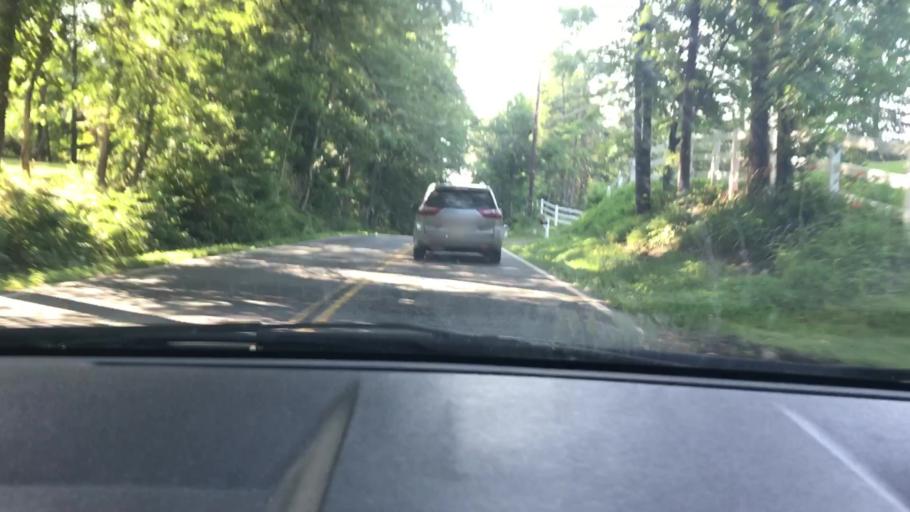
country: US
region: Virginia
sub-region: Fairfax County
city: Great Falls
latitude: 38.9729
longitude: -77.2525
